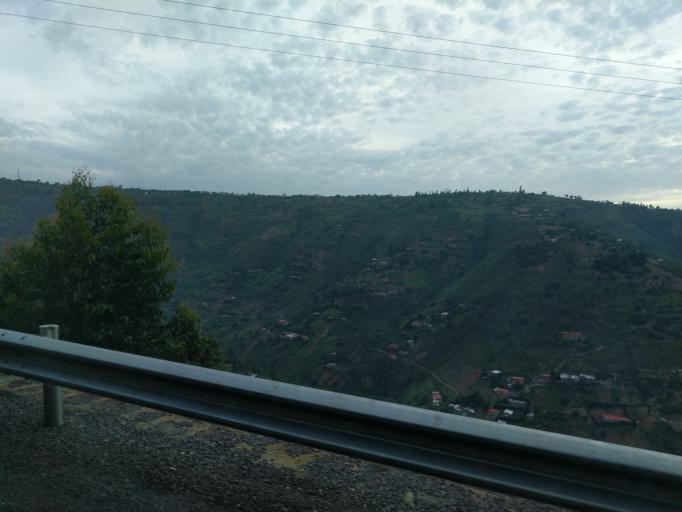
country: RW
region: Kigali
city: Kigali
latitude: -1.9359
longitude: 30.0266
